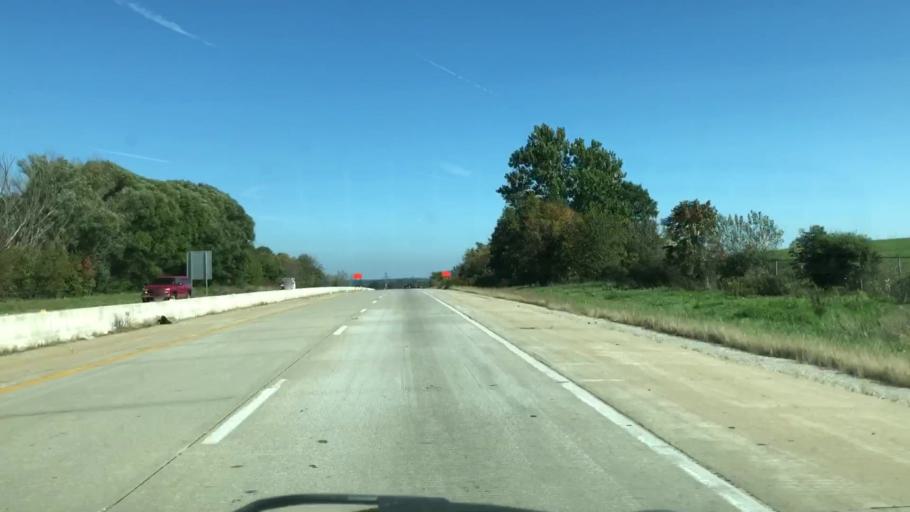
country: US
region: Indiana
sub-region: Elkhart County
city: Elkhart
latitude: 41.6376
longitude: -85.9769
